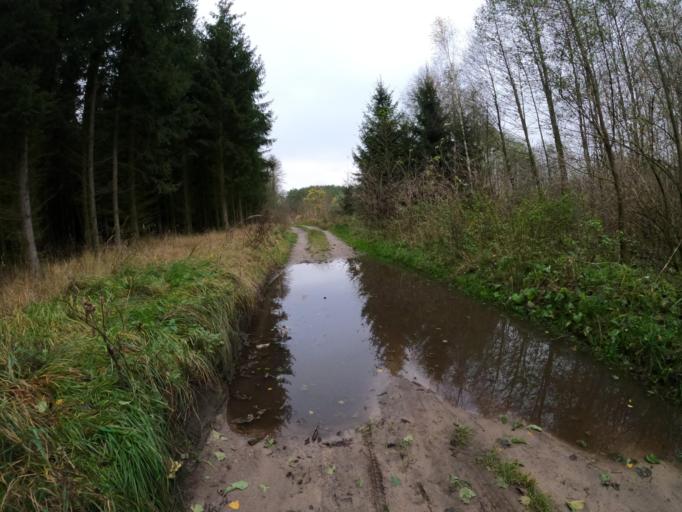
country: PL
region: West Pomeranian Voivodeship
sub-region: Powiat walecki
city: Miroslawiec
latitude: 53.3064
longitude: 16.1096
